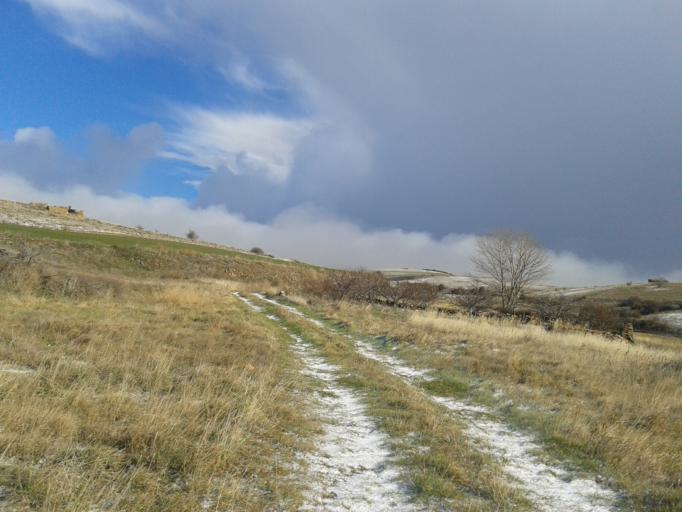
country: ES
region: Aragon
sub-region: Provincia de Teruel
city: Bea
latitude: 40.9895
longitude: -1.1632
